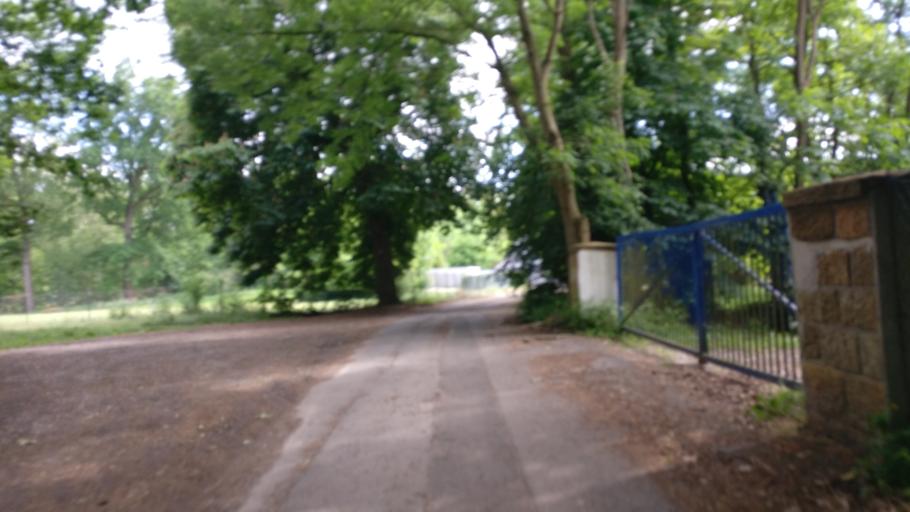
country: DE
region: North Rhine-Westphalia
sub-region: Regierungsbezirk Detmold
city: Lage
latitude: 52.0142
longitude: 8.7596
